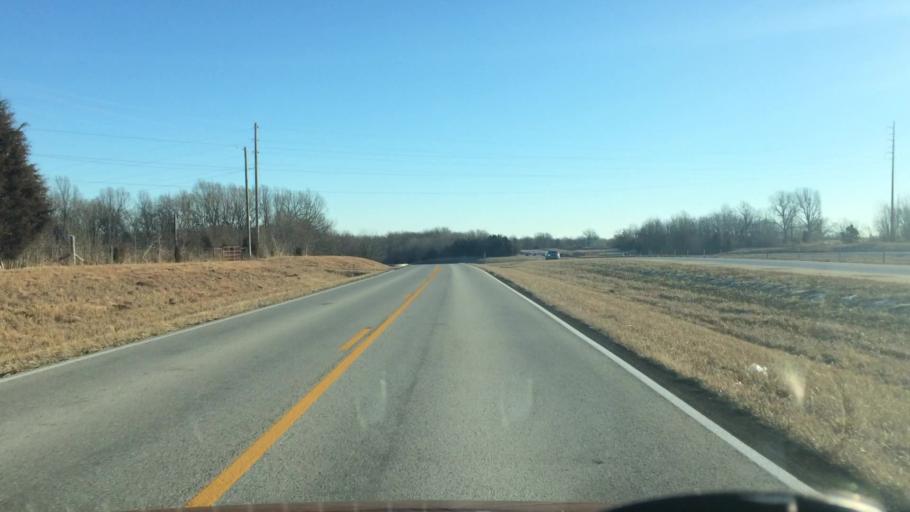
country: US
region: Missouri
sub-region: Greene County
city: Strafford
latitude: 37.2736
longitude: -93.0543
